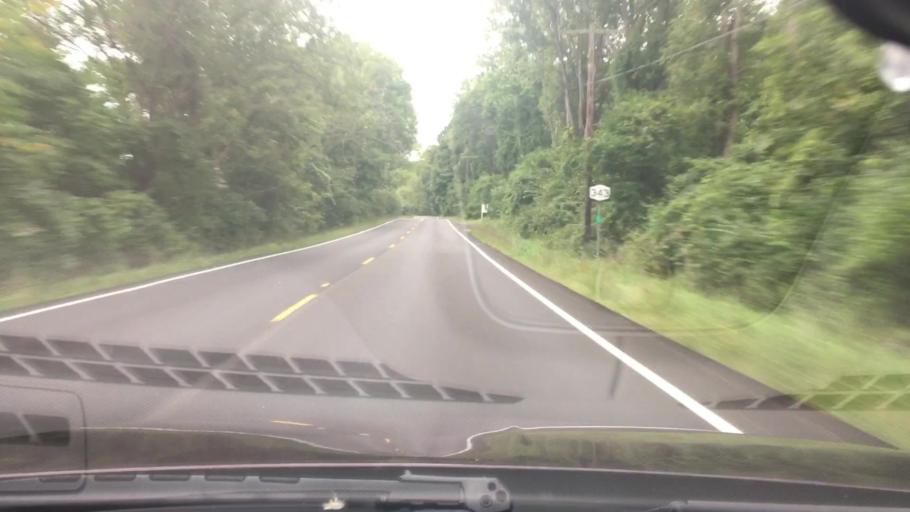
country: US
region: New York
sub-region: Dutchess County
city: Dover Plains
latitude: 41.8637
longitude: -73.5064
